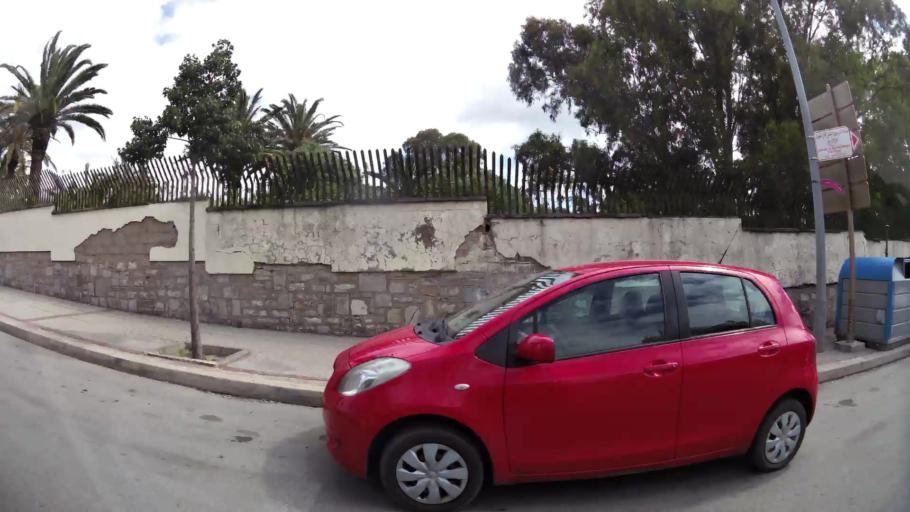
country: MA
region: Tanger-Tetouan
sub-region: Tanger-Assilah
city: Tangier
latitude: 35.7787
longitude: -5.8250
